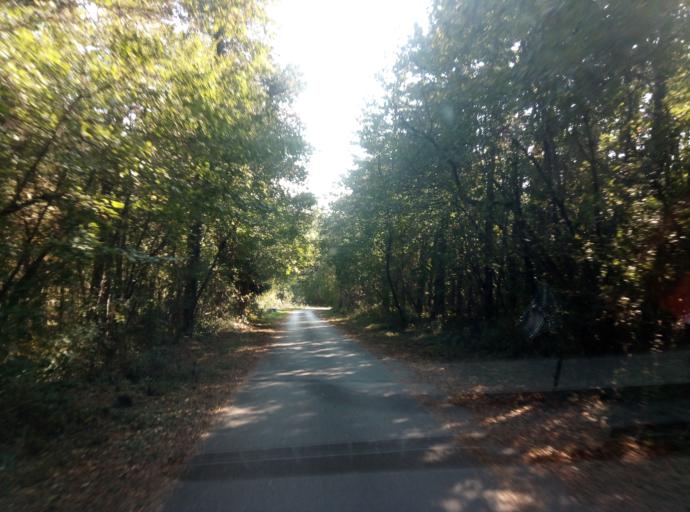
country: SI
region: Ajdovscina
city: Lokavec
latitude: 45.8194
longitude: 13.8524
